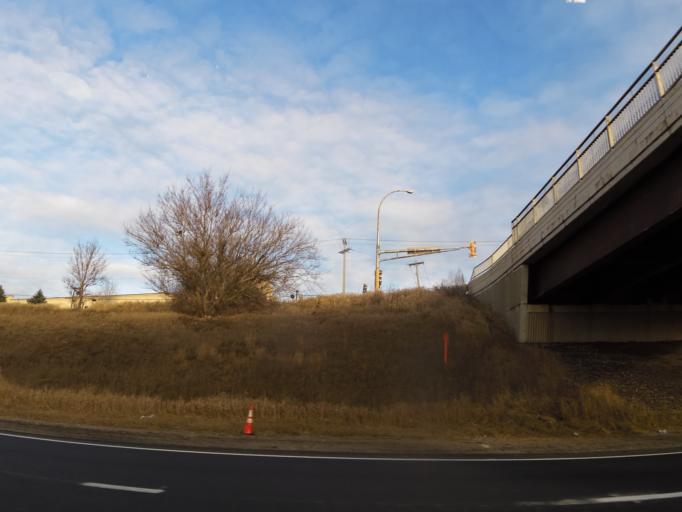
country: US
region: Minnesota
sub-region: Ramsey County
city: Lauderdale
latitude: 45.0148
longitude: -93.1871
